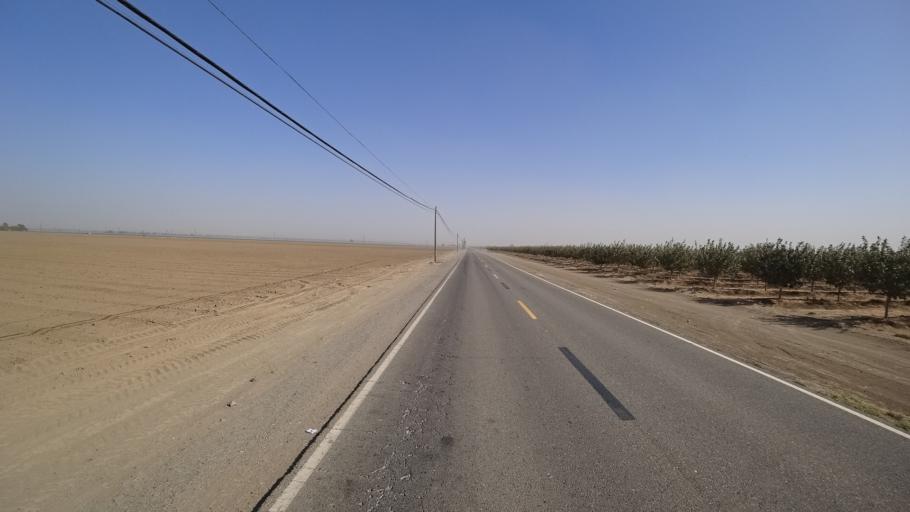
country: US
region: California
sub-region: Yolo County
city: Woodland
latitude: 38.7346
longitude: -121.7340
